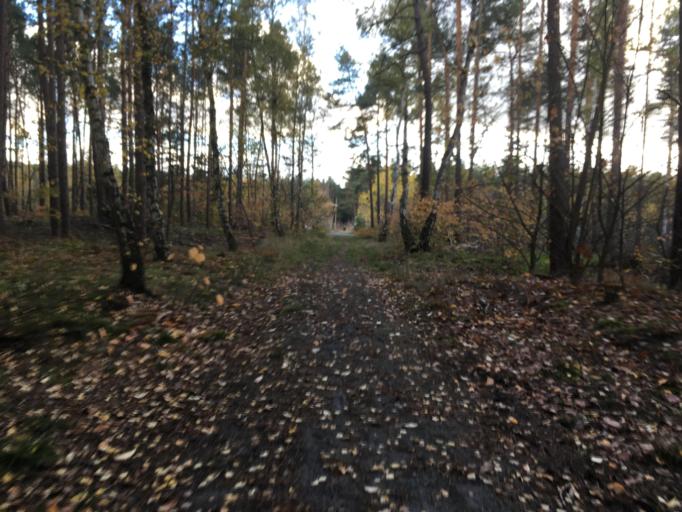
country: DE
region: Brandenburg
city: Birkenwerder
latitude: 52.6934
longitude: 13.3368
